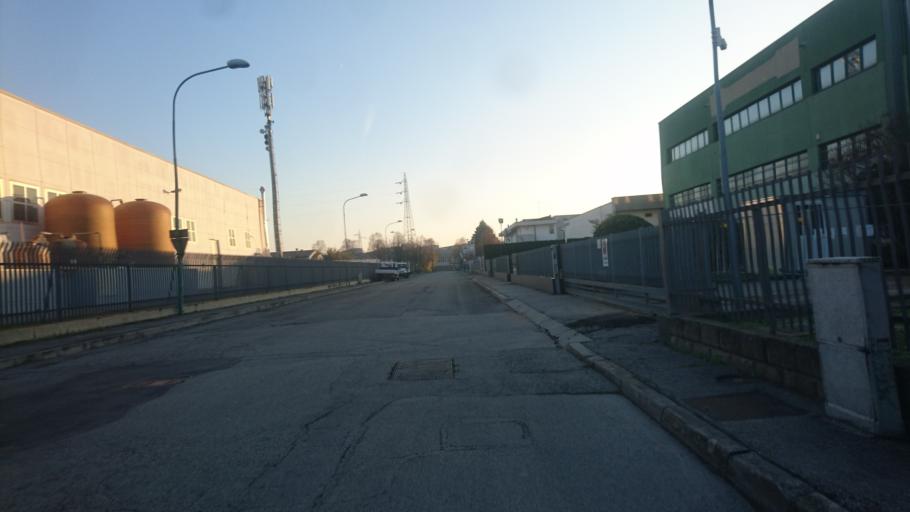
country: IT
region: Veneto
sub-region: Provincia di Padova
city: Caselle
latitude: 45.4058
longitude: 11.8198
